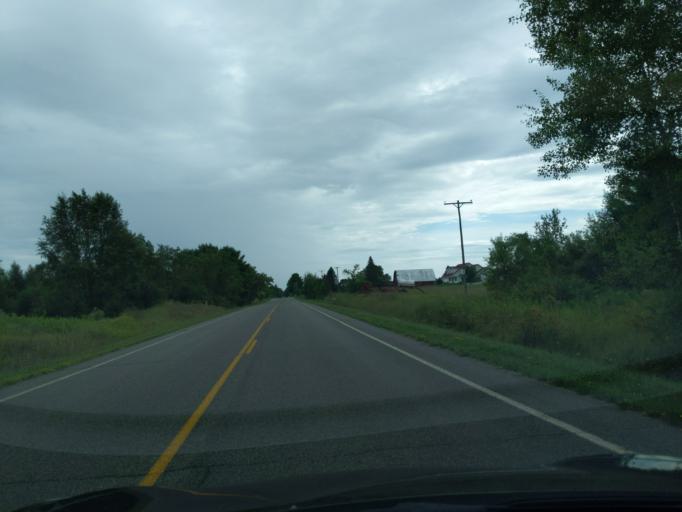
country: US
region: Michigan
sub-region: Clare County
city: Harrison
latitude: 44.0114
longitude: -84.9492
